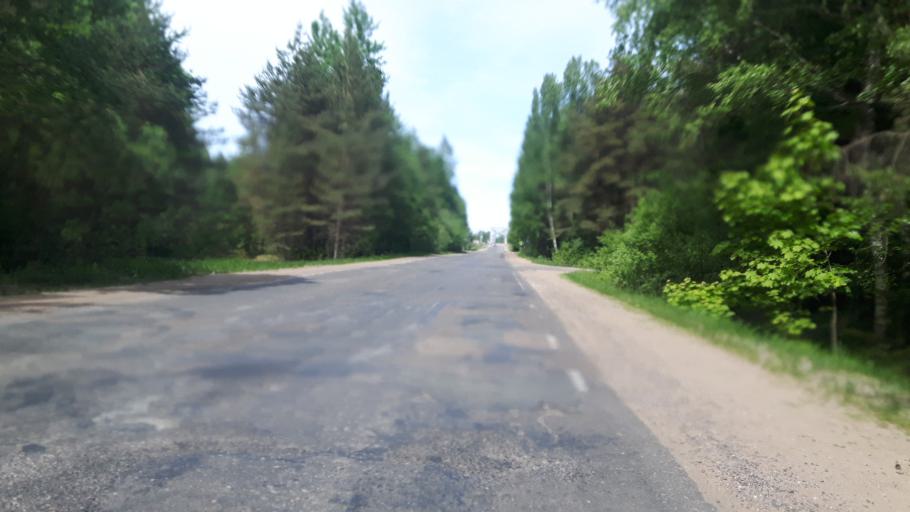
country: RU
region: Leningrad
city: Ust'-Luga
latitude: 59.6491
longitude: 28.2625
